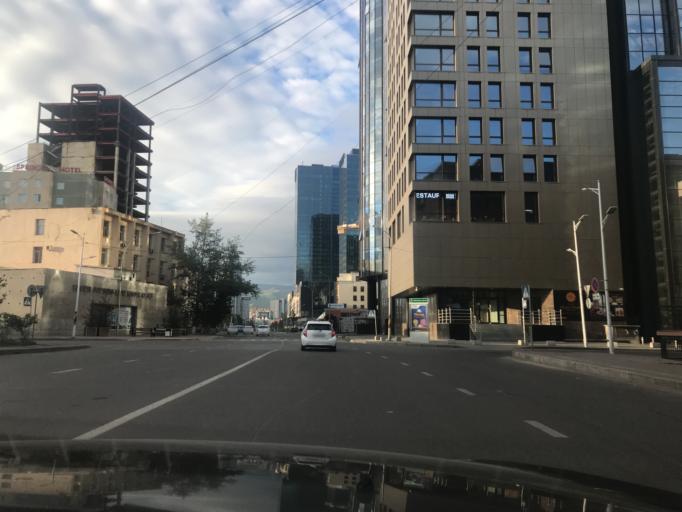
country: MN
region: Ulaanbaatar
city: Ulaanbaatar
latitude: 47.9166
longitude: 106.9201
